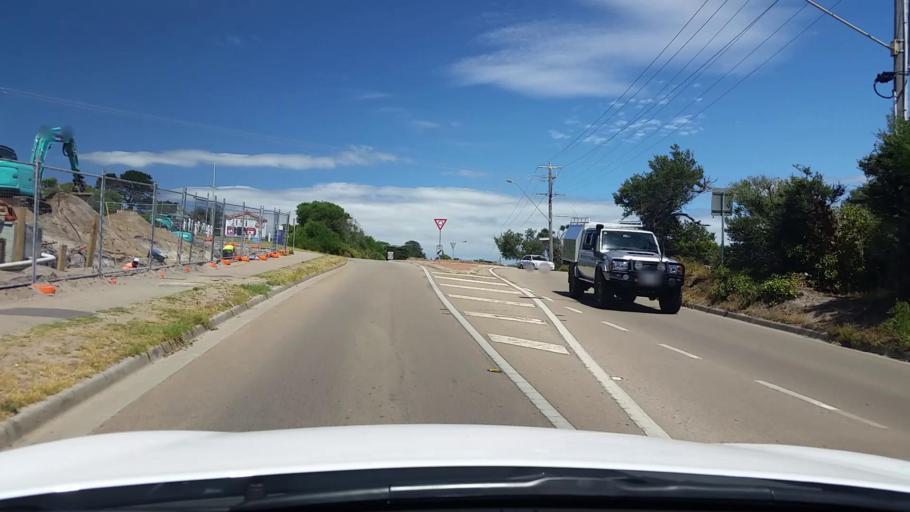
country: AU
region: Victoria
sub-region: Mornington Peninsula
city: Mount Martha
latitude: -38.2683
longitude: 145.0118
